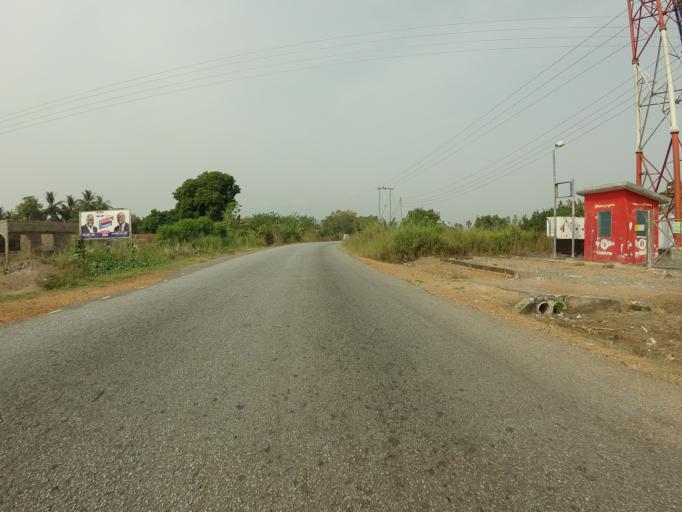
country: GH
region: Volta
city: Ho
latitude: 6.5727
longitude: 0.3639
